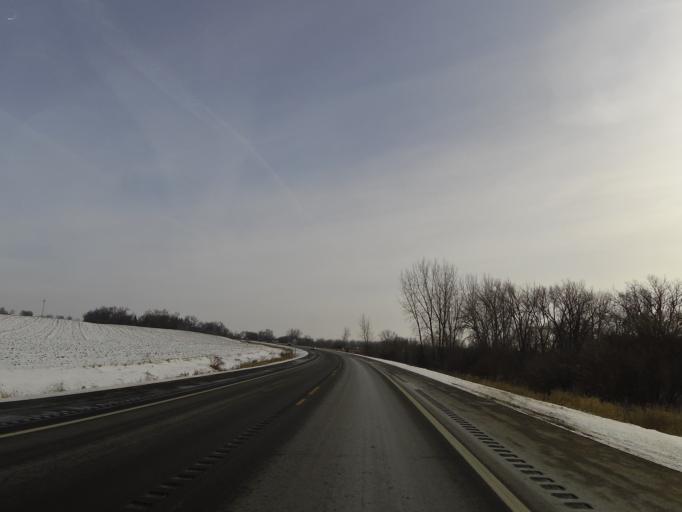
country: US
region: Minnesota
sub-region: McLeod County
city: Hutchinson
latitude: 44.8956
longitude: -94.4290
